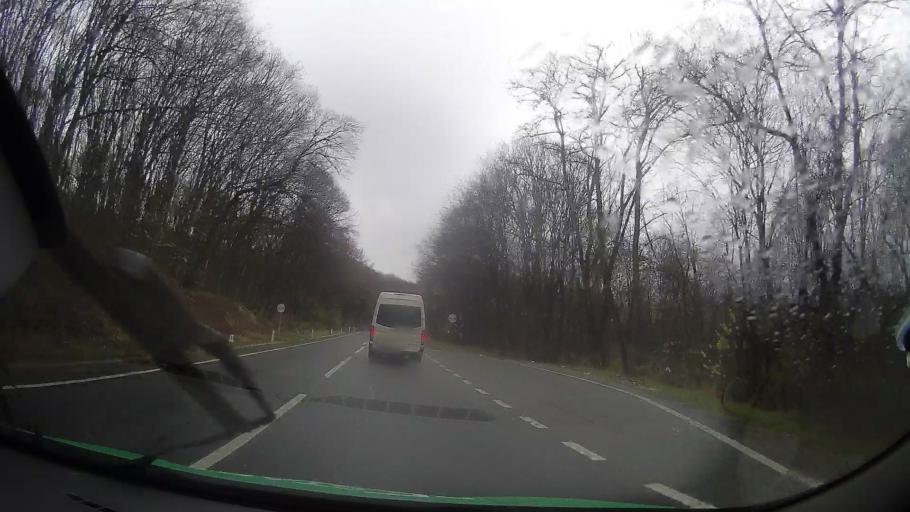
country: RO
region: Bistrita-Nasaud
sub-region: Comuna Galatii Bistritei
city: Galatii Bistritei
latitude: 47.0372
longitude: 24.4212
